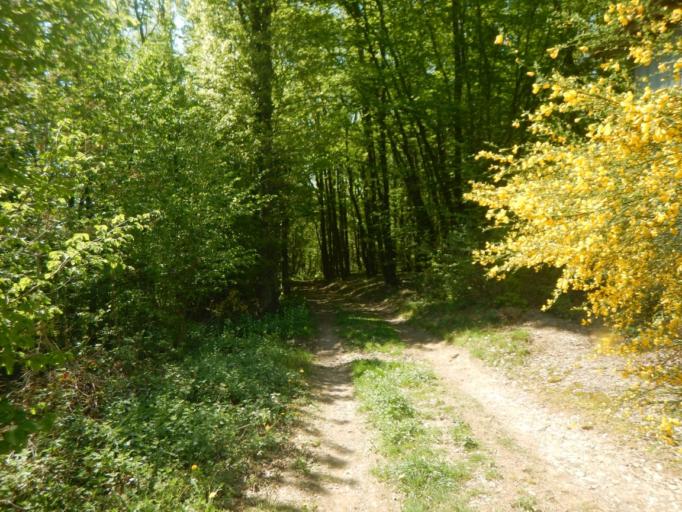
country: LU
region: Diekirch
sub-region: Canton de Diekirch
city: Bourscheid
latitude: 49.9070
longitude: 6.0900
